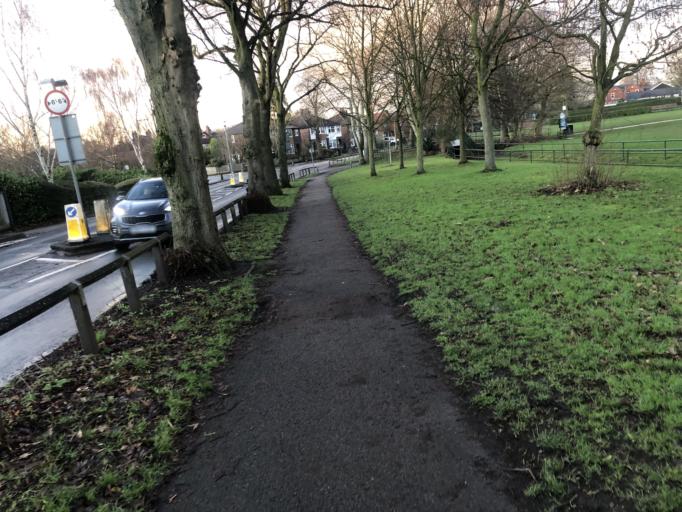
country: GB
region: England
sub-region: Trafford
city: Urmston
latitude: 53.4464
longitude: -2.3692
